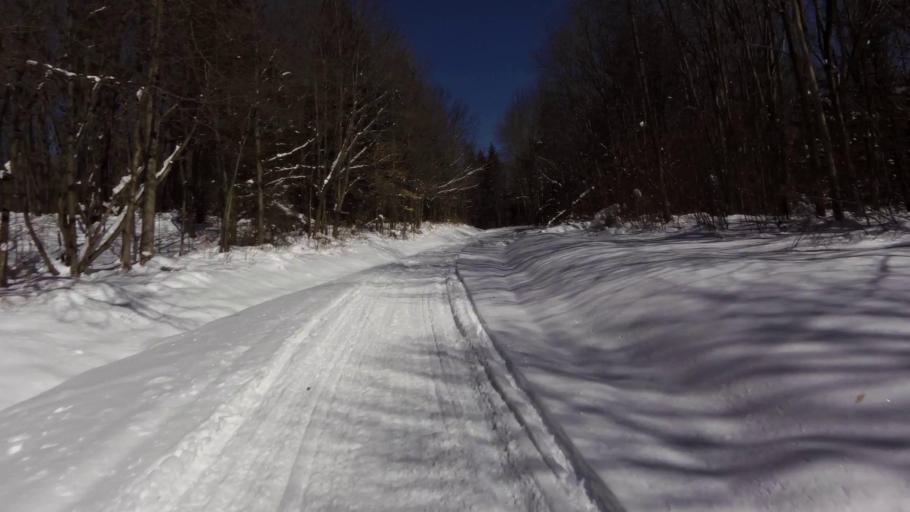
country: US
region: New York
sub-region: Allegany County
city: Cuba
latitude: 42.2972
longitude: -78.2417
